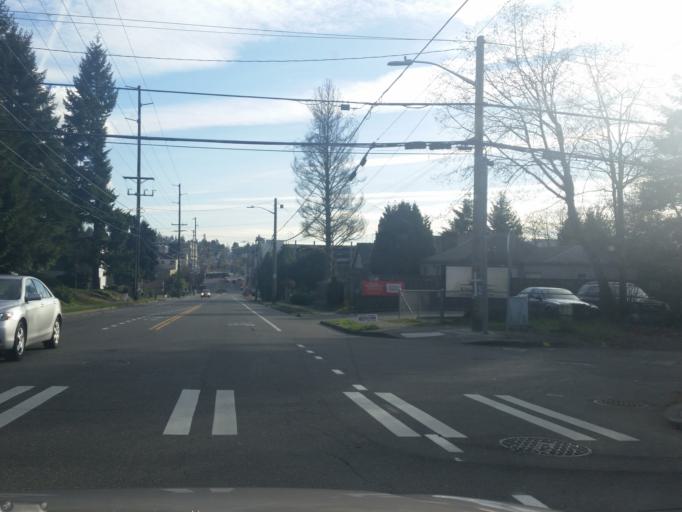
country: US
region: Washington
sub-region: King County
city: Shoreline
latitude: 47.7125
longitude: -122.3235
